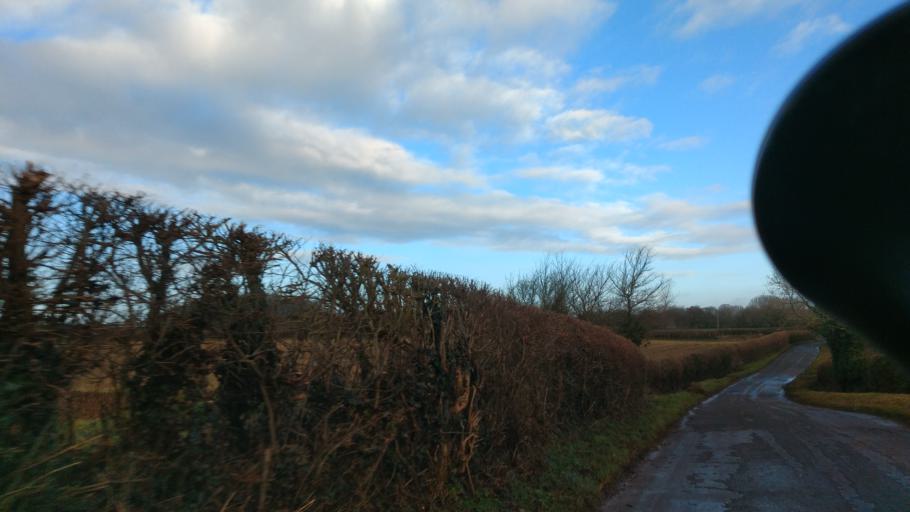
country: GB
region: England
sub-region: Wiltshire
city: Corsham
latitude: 51.4602
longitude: -2.1622
